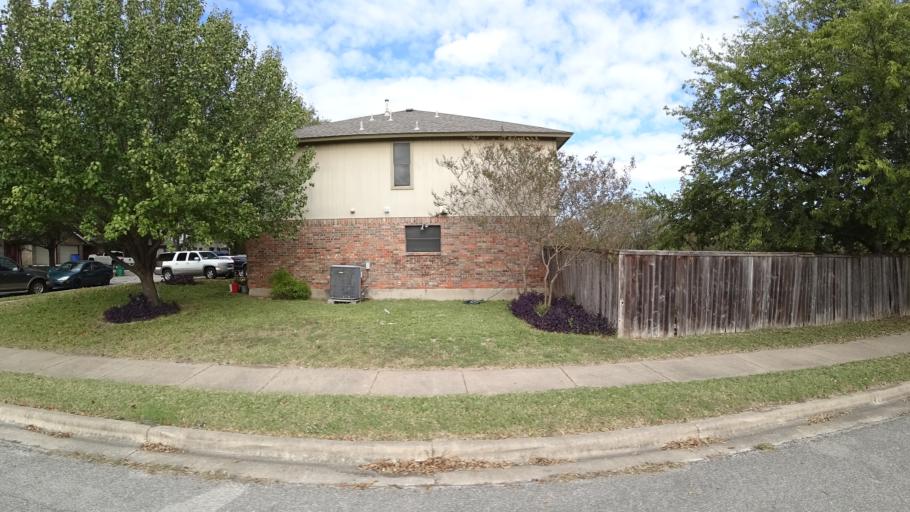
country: US
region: Texas
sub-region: Travis County
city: Pflugerville
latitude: 30.4409
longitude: -97.6352
